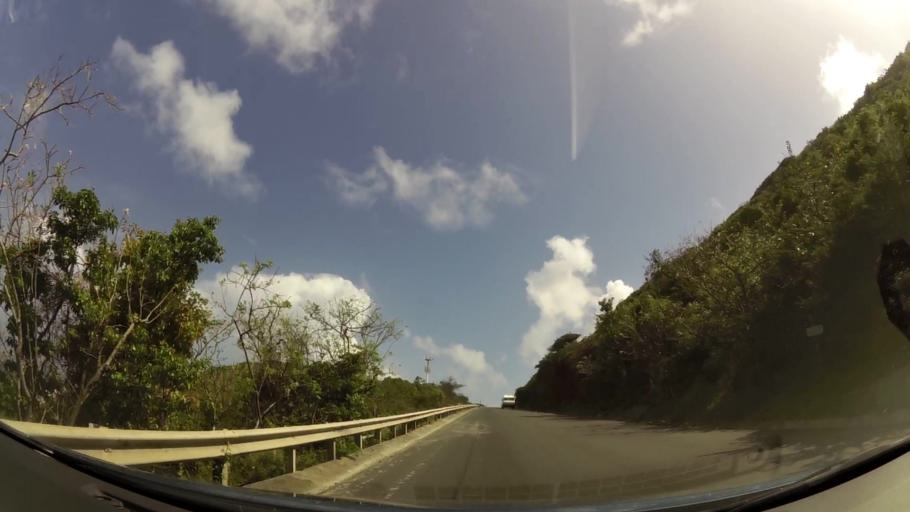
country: KN
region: Saint George Basseterre
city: Basseterre
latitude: 17.2815
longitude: -62.6806
